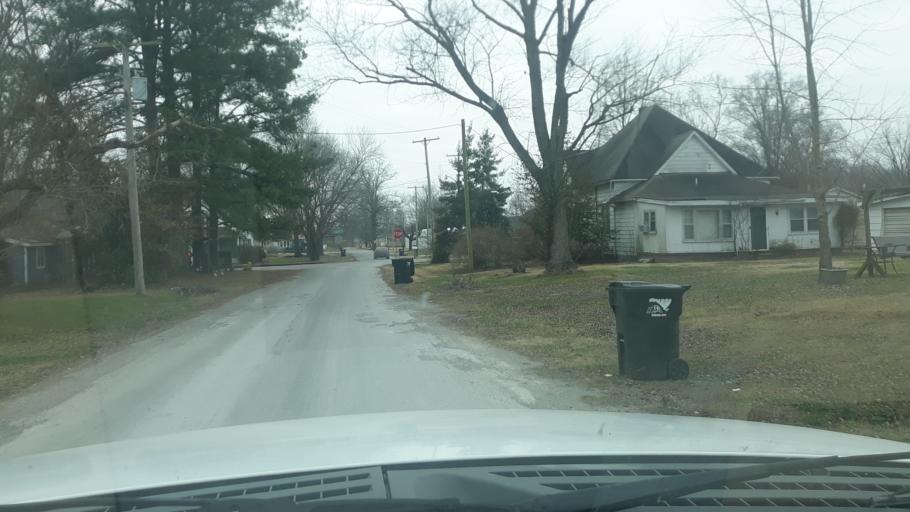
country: US
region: Illinois
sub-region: Saline County
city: Harrisburg
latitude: 37.8405
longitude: -88.6054
